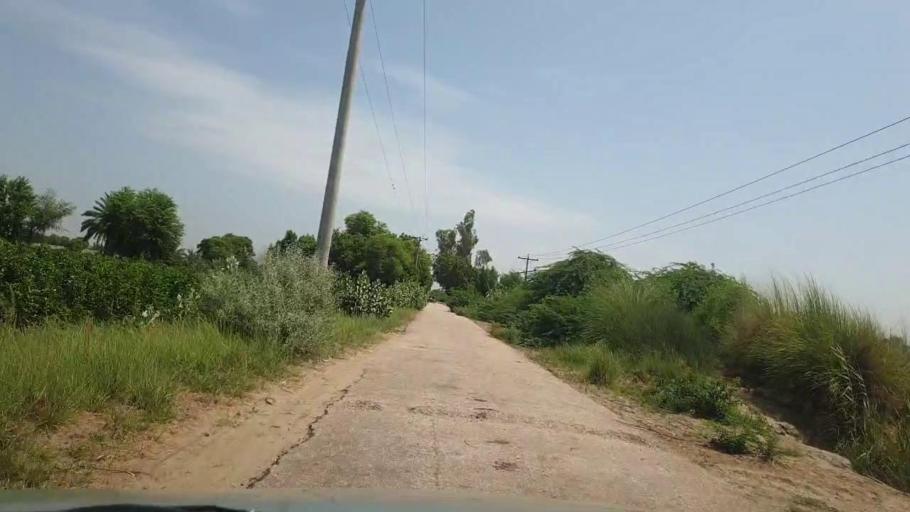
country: PK
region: Sindh
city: Kot Diji
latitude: 27.1248
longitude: 68.9975
